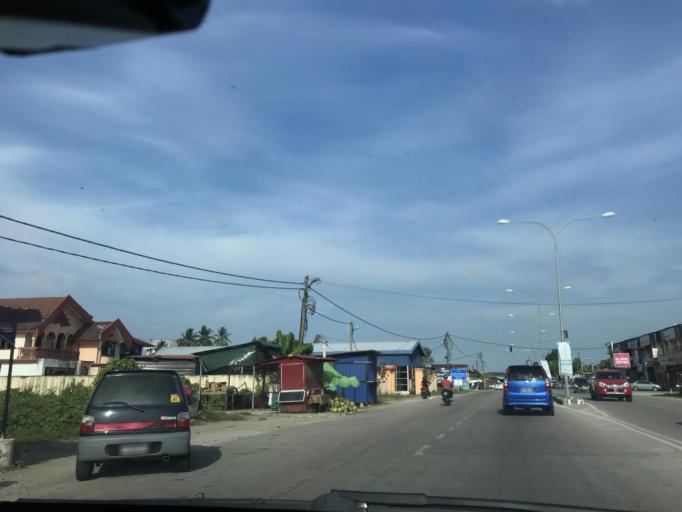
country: MY
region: Kelantan
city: Kota Bharu
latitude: 6.1207
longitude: 102.2857
